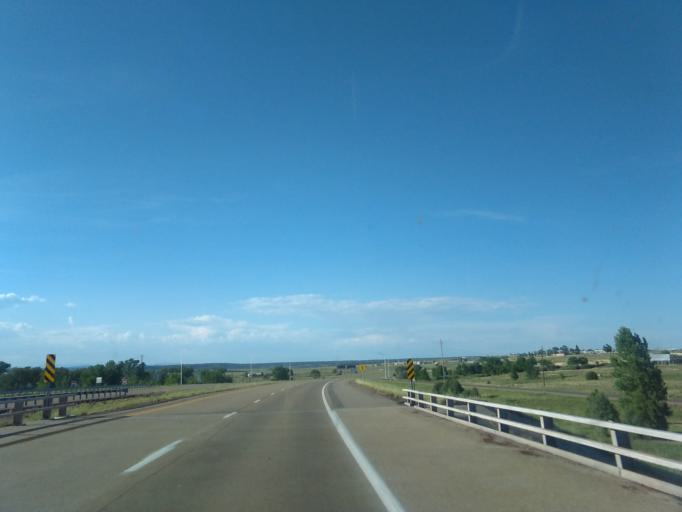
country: US
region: New Mexico
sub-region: San Miguel County
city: Las Vegas
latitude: 35.6248
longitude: -105.2033
